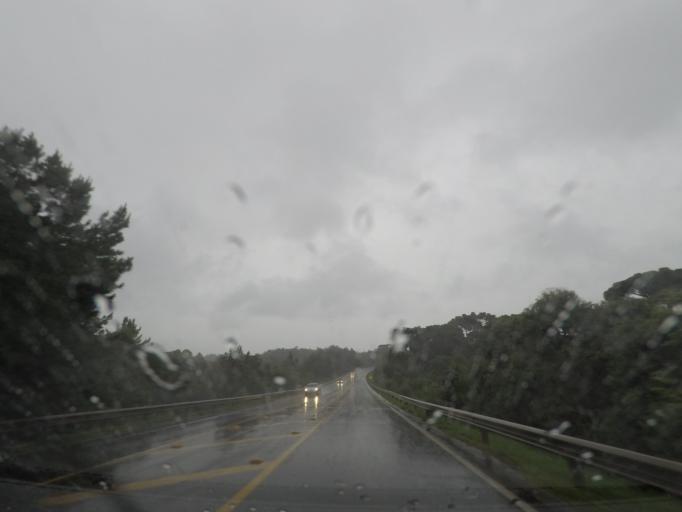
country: BR
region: Parana
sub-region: Almirante Tamandare
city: Almirante Tamandare
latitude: -25.3560
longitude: -49.3089
